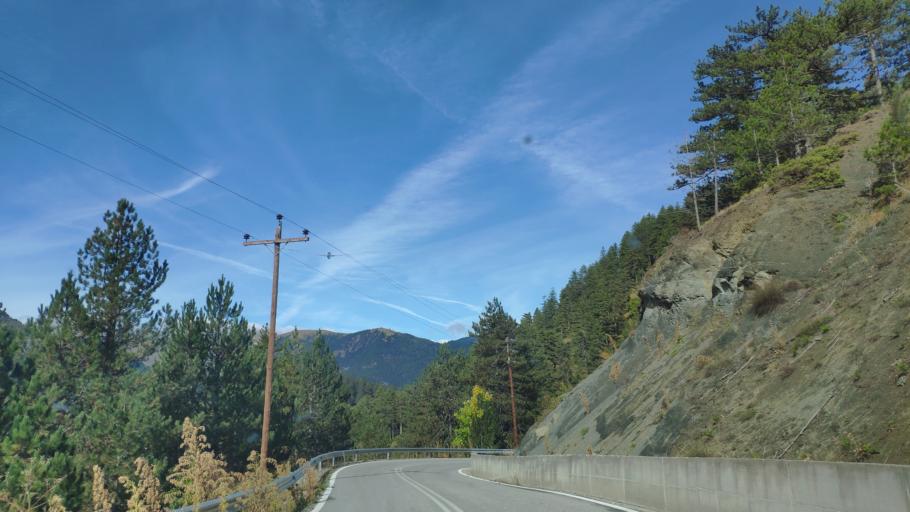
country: AL
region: Korce
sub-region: Rrethi i Devollit
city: Miras
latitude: 40.3980
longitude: 20.9022
